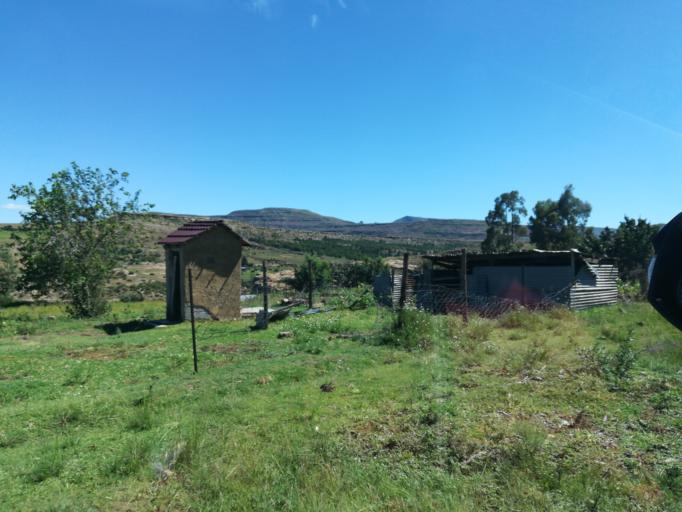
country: LS
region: Quthing
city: Quthing
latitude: -30.3313
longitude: 27.5317
